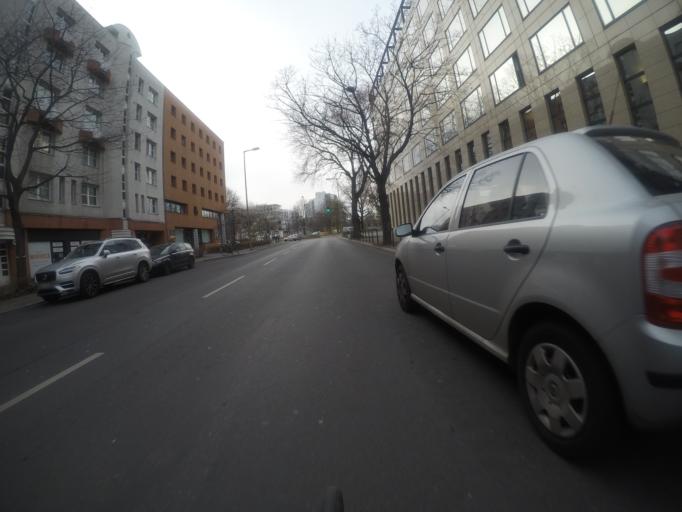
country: DE
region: Berlin
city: Tiergarten Bezirk
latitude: 52.5052
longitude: 13.3549
